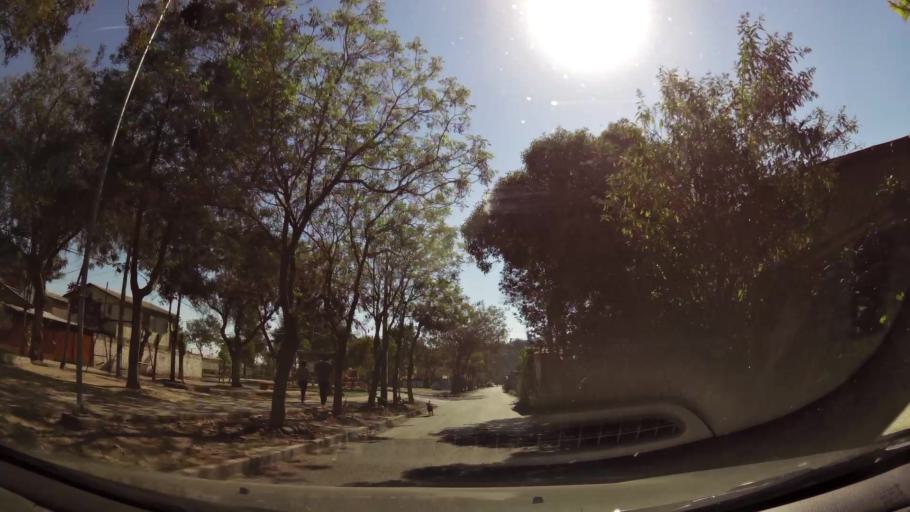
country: CL
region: Santiago Metropolitan
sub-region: Provincia de Maipo
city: San Bernardo
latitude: -33.6119
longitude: -70.7083
